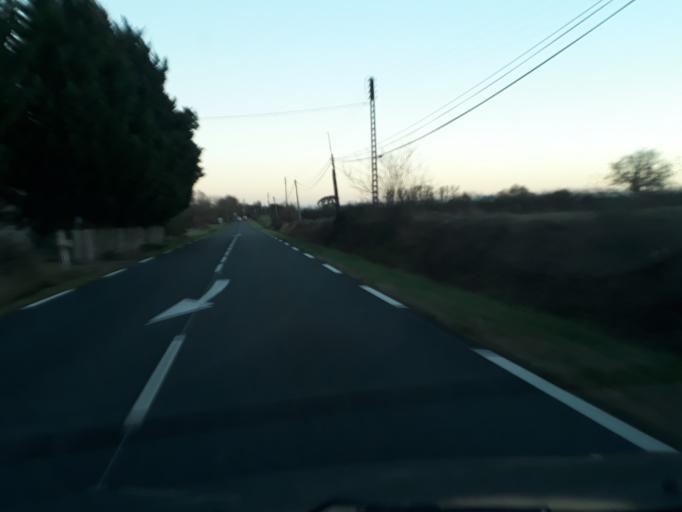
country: FR
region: Midi-Pyrenees
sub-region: Departement de la Haute-Garonne
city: Fontenilles
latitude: 43.5418
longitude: 1.1609
